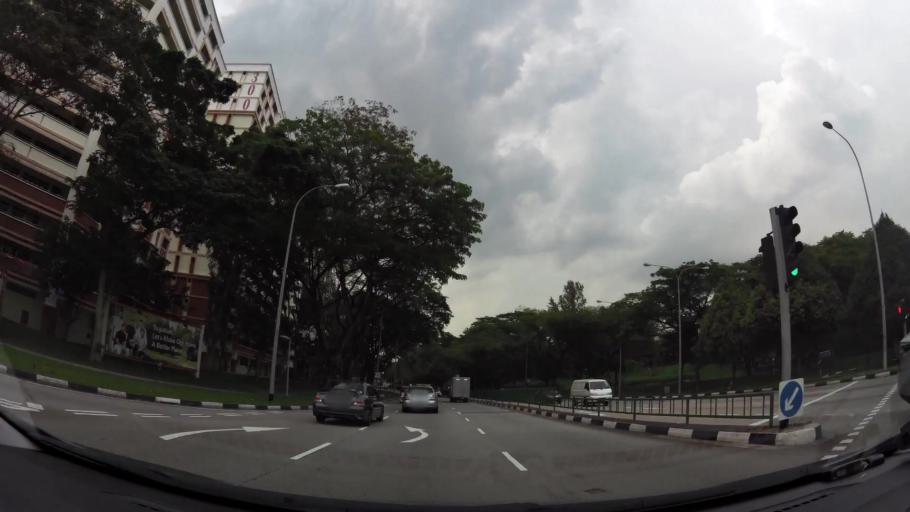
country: MY
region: Johor
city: Kampung Pasir Gudang Baru
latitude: 1.4451
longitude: 103.8235
